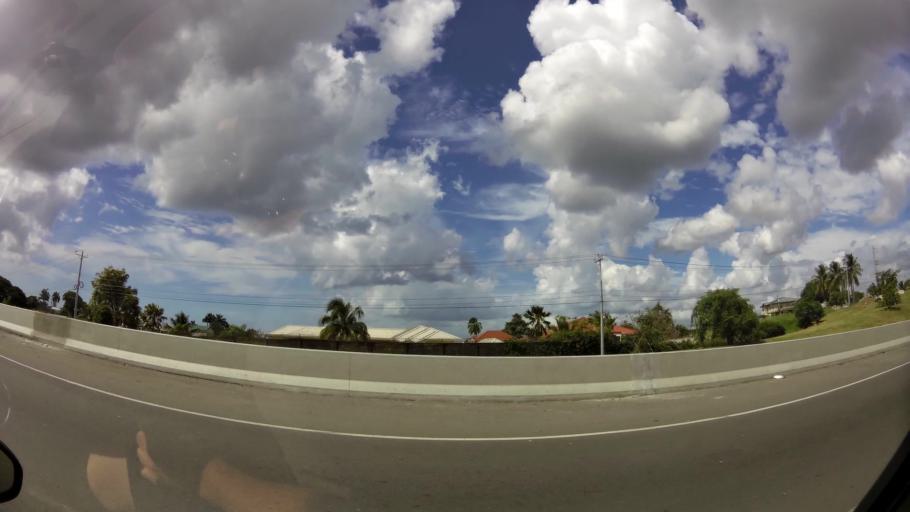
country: TT
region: City of San Fernando
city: San Fernando
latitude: 10.2537
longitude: -61.4815
